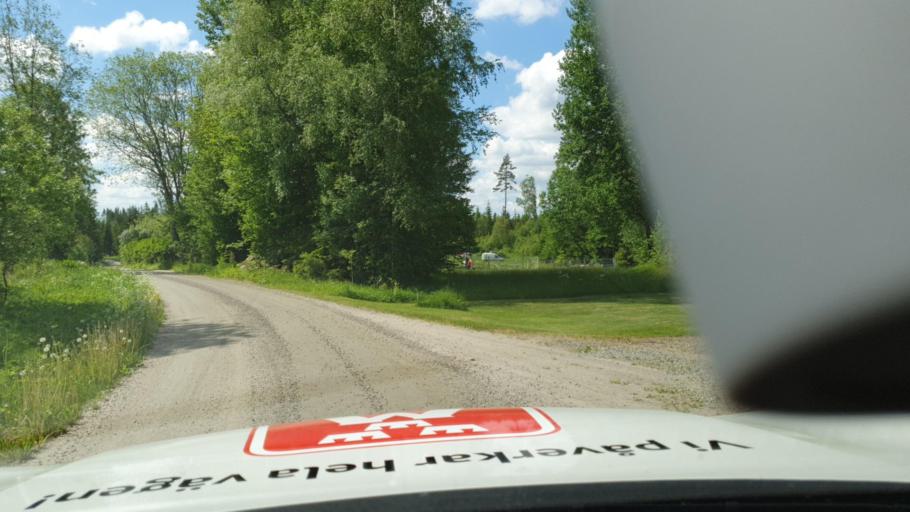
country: SE
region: Vaestra Goetaland
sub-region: Falkopings Kommun
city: Falkoeping
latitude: 58.0294
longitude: 13.6817
